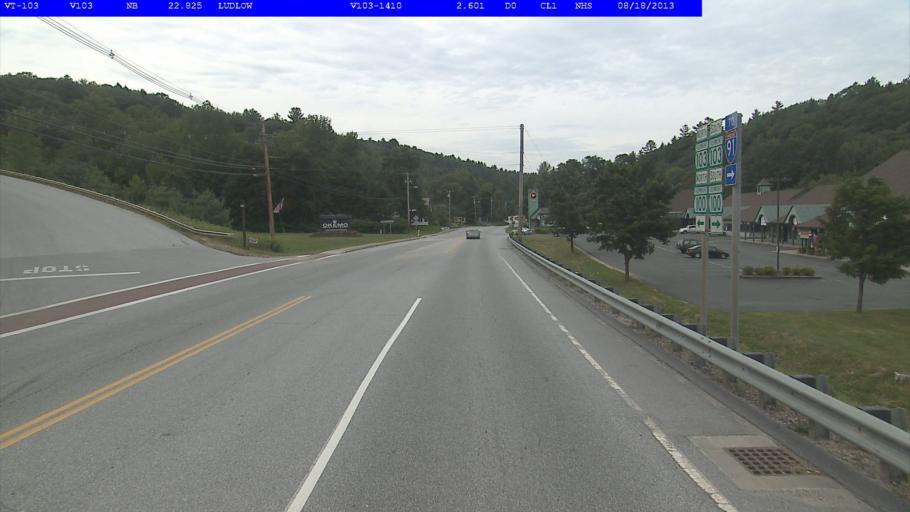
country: US
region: Vermont
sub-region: Windsor County
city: Chester
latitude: 43.3997
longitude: -72.7065
